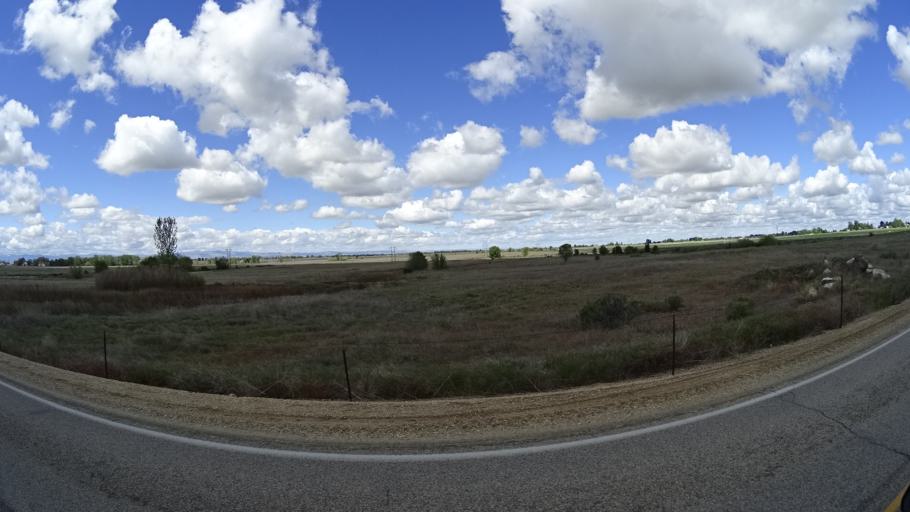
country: US
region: Idaho
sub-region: Ada County
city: Kuna
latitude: 43.5156
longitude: -116.3443
